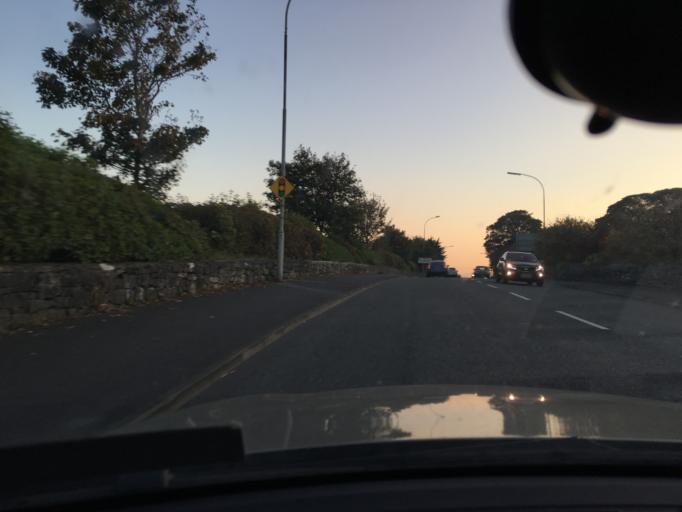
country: IE
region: Connaught
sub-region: County Galway
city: Gaillimh
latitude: 53.2691
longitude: -9.0872
